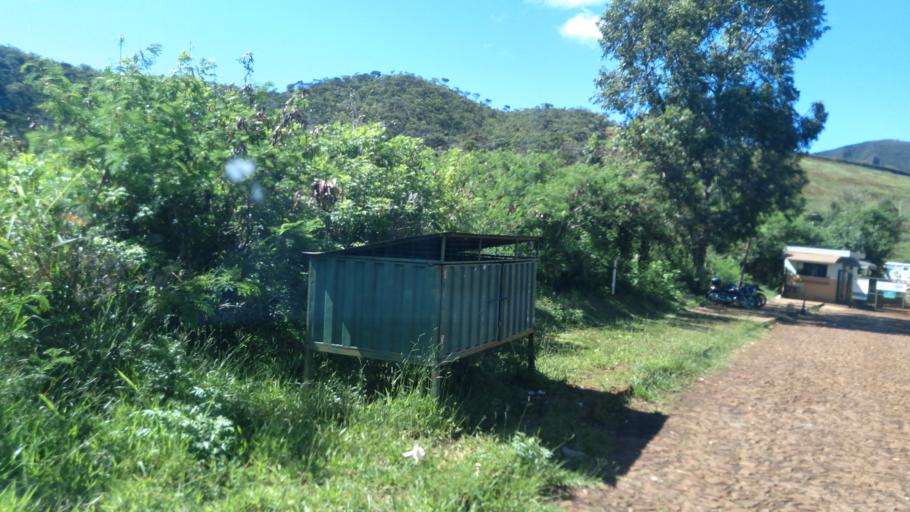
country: BR
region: Minas Gerais
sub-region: Belo Horizonte
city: Belo Horizonte
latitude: -19.9331
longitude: -43.8822
